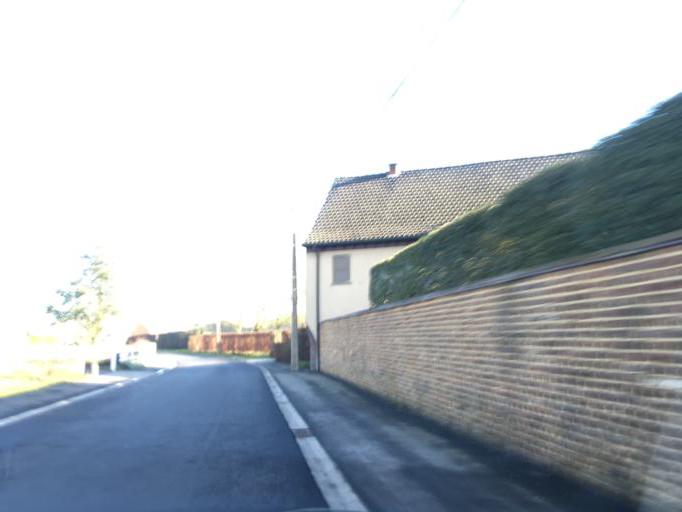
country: BE
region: Flanders
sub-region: Provincie West-Vlaanderen
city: Roeselare
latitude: 50.9189
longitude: 3.1460
